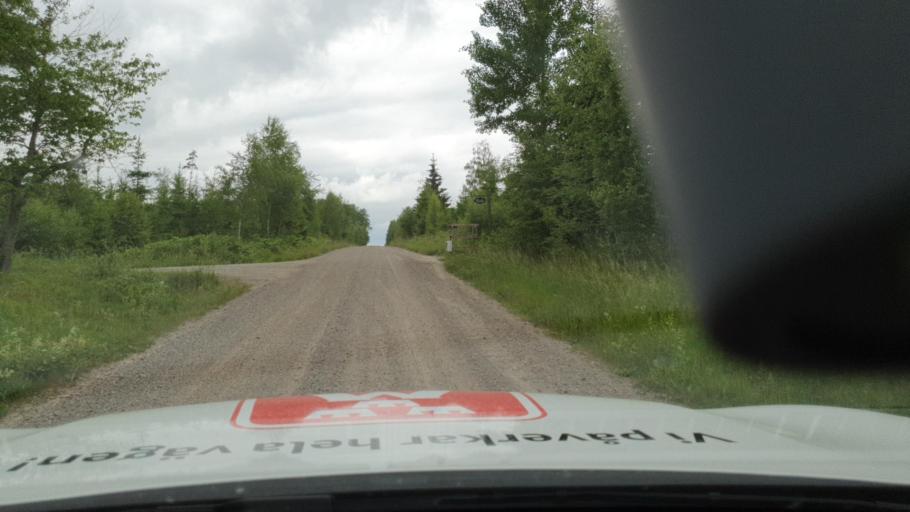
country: SE
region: Vaestra Goetaland
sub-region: Tidaholms Kommun
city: Tidaholm
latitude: 58.1601
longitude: 14.0579
